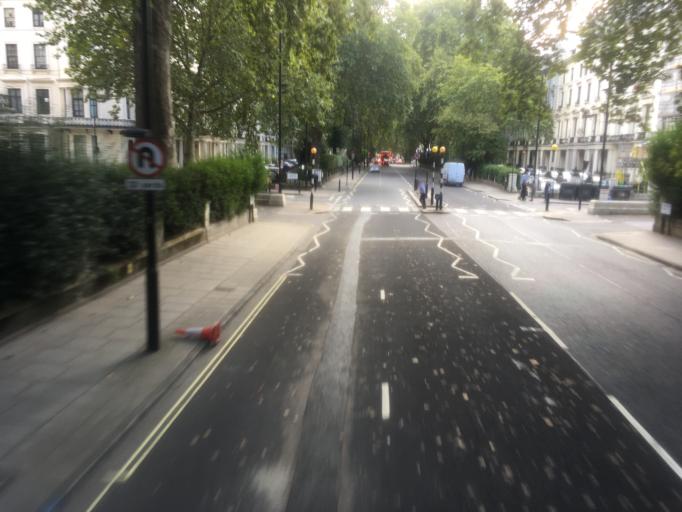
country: GB
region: England
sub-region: Greater London
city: Bayswater
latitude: 51.5159
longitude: -0.1797
